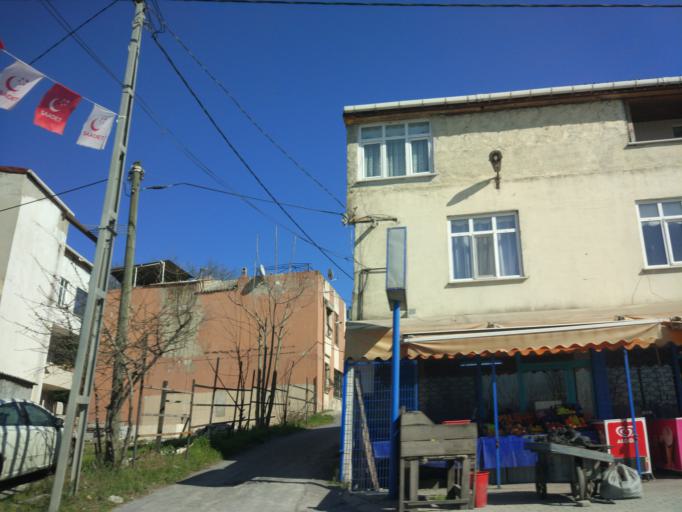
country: TR
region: Istanbul
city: Basaksehir
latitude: 41.0542
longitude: 28.7501
